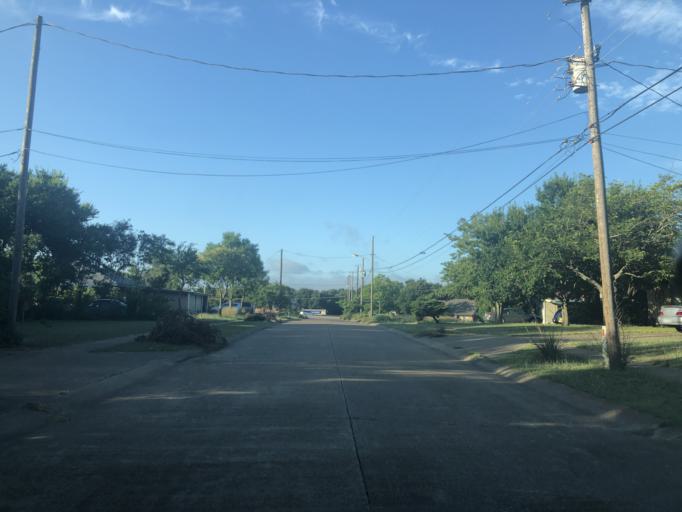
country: US
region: Texas
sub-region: Dallas County
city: Duncanville
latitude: 32.6675
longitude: -96.9522
